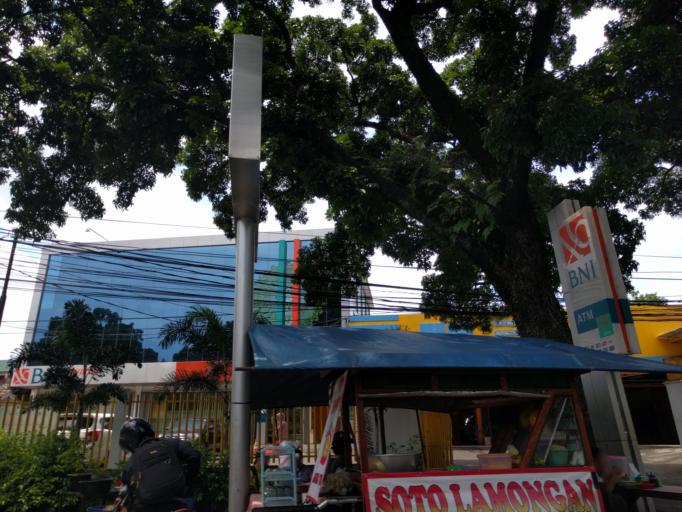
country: ID
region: West Java
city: Bogor
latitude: -6.5754
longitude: 106.8079
